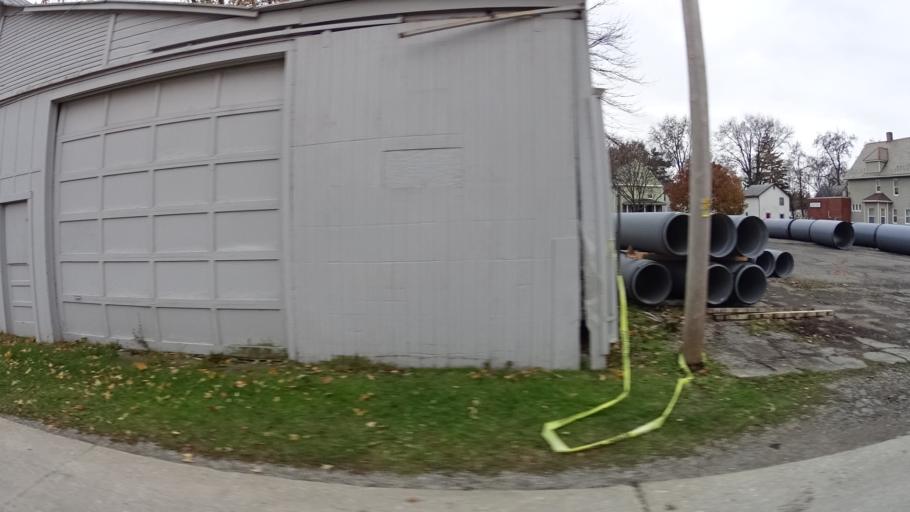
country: US
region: Ohio
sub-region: Lorain County
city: Elyria
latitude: 41.3636
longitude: -82.1048
